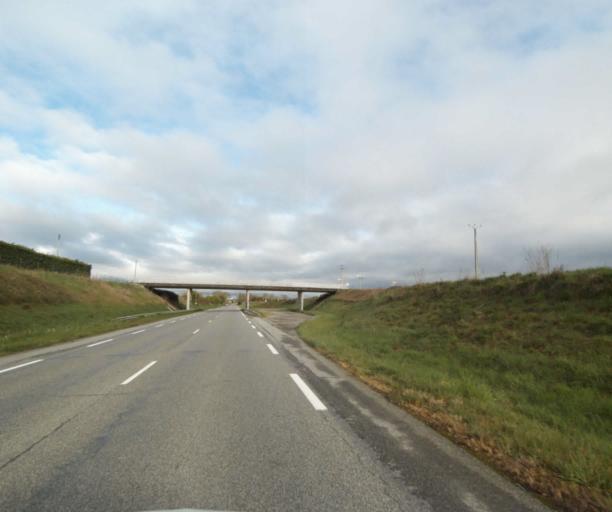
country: FR
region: Midi-Pyrenees
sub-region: Departement de l'Ariege
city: Saverdun
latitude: 43.2400
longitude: 1.5863
